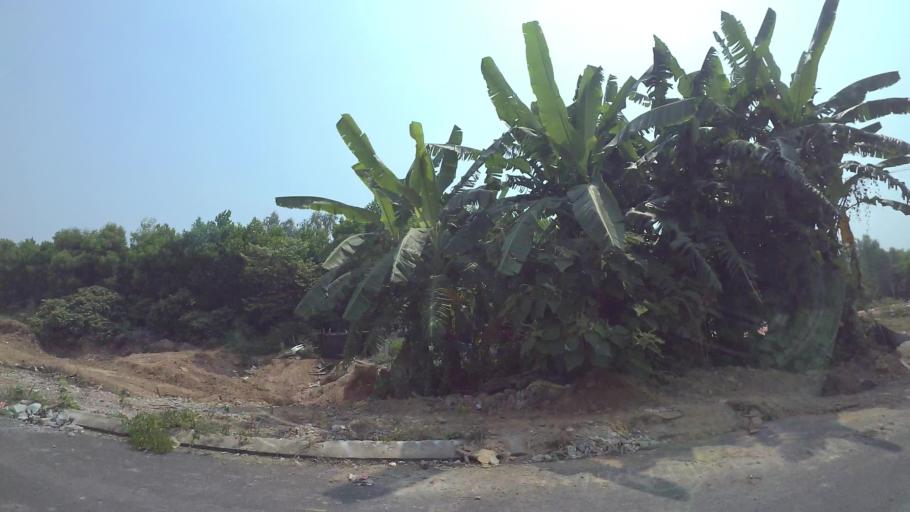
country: VN
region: Da Nang
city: Cam Le
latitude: 15.9817
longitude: 108.2202
